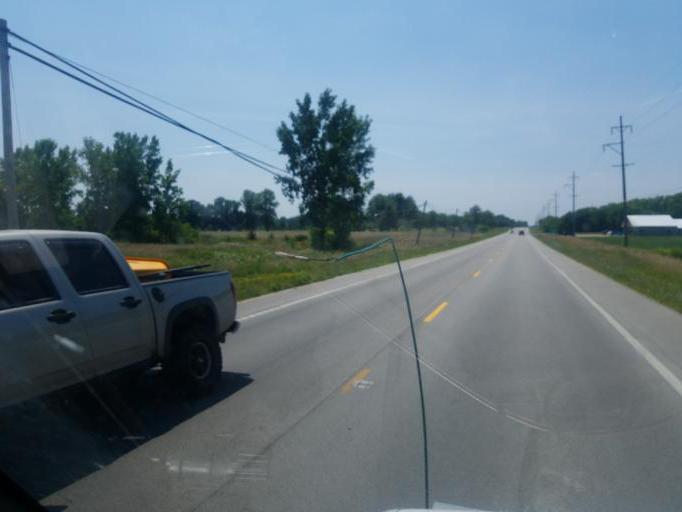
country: US
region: Ohio
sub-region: Auglaize County
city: Saint Marys
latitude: 40.5511
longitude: -84.4720
